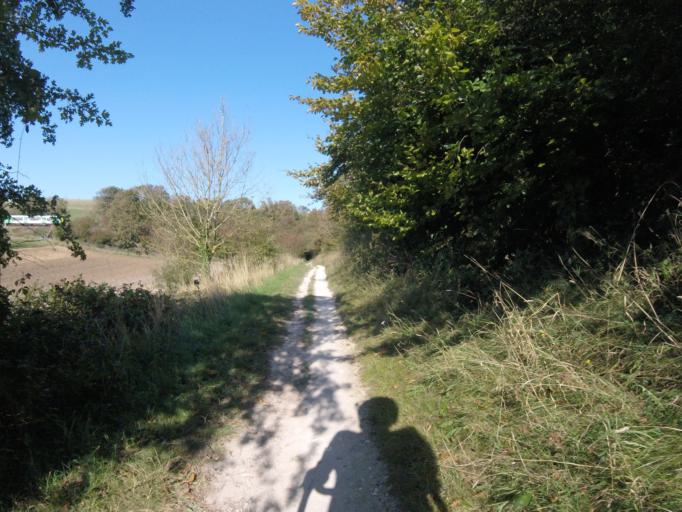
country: GB
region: England
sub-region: Brighton and Hove
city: Rottingdean
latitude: 50.8634
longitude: -0.0488
